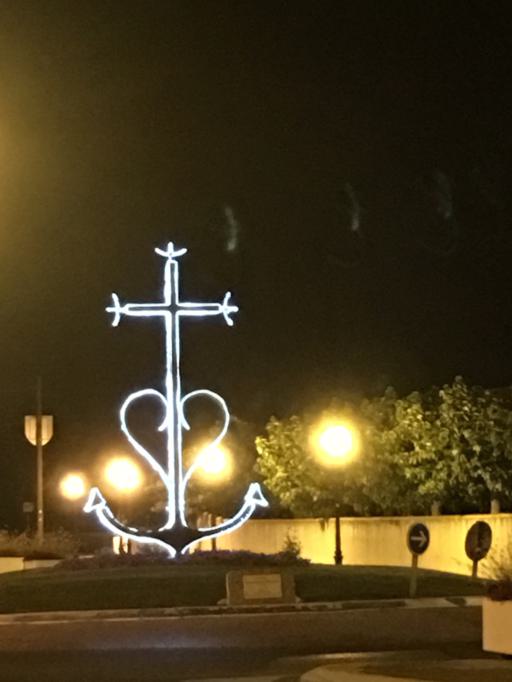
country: FR
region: Provence-Alpes-Cote d'Azur
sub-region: Departement des Bouches-du-Rhone
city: Saintes-Maries-de-la-Mer
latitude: 43.4557
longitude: 4.4271
